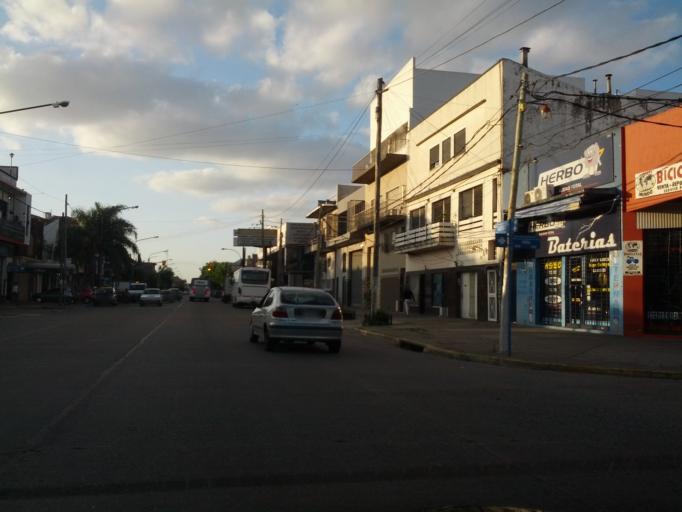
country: AR
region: Buenos Aires
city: San Justo
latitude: -34.6504
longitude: -58.5348
